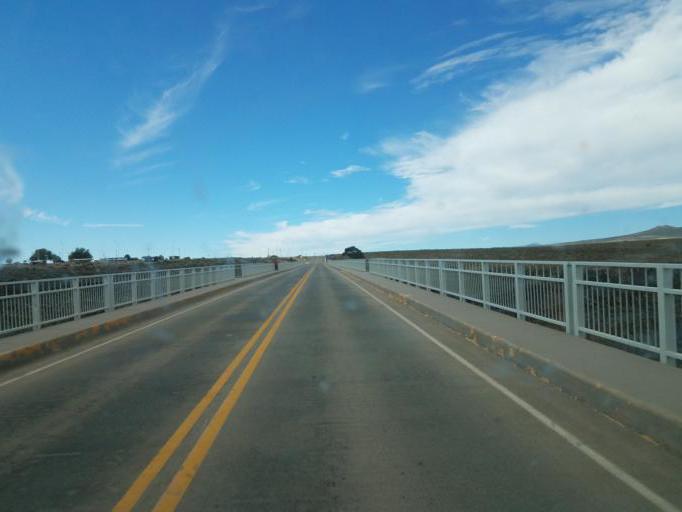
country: US
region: New Mexico
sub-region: Taos County
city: Arroyo Seco
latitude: 36.4760
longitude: -105.7325
